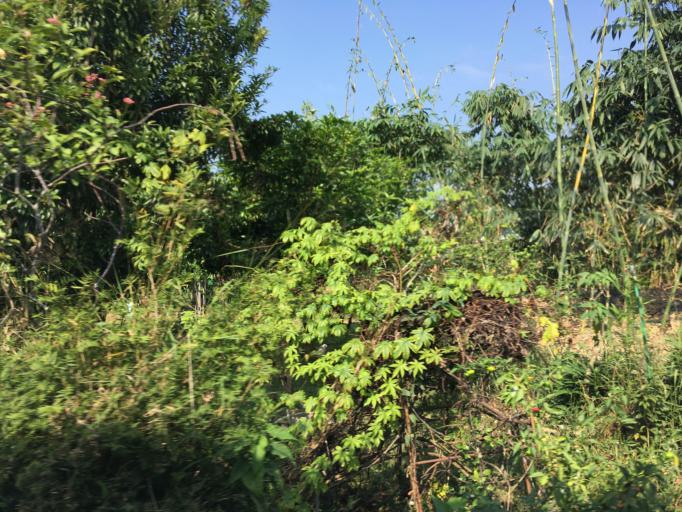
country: TW
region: Taiwan
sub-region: Chiayi
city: Jiayi Shi
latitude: 23.4975
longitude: 120.4813
